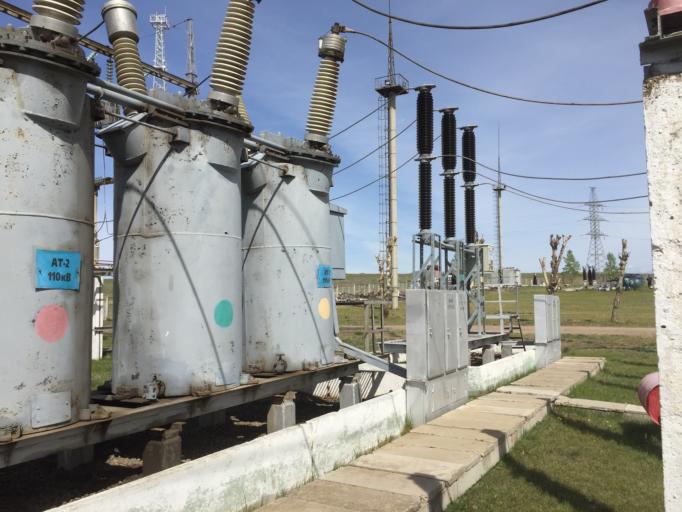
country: MN
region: Darhan Uul
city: Darhan
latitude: 49.3977
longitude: 105.9469
